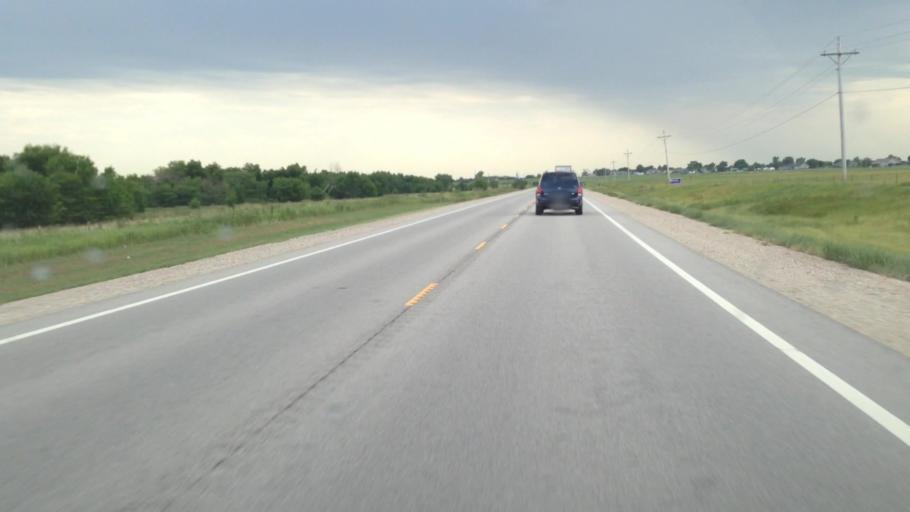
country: US
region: Kansas
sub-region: Coffey County
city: Burlington
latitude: 38.2814
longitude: -95.7382
